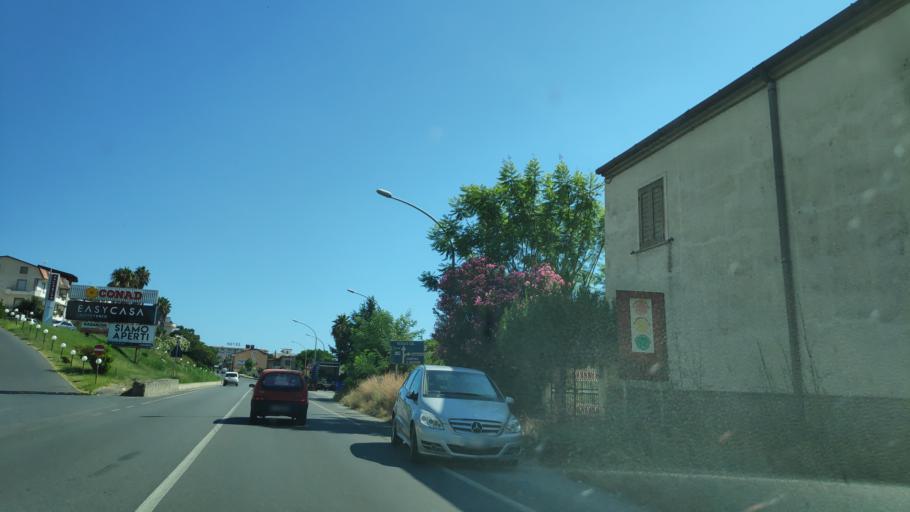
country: IT
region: Calabria
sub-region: Provincia di Cosenza
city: Campora San Giovanni
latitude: 39.0704
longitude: 16.0919
